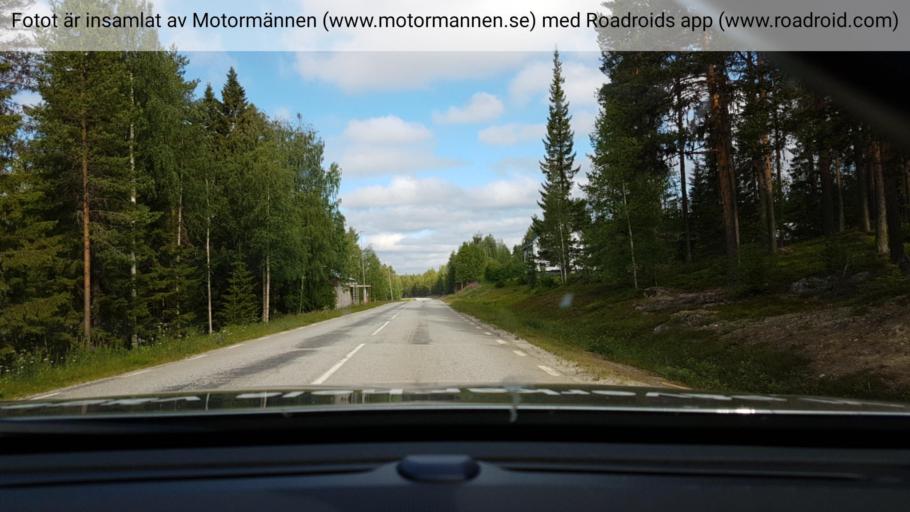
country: SE
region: Vaesterbotten
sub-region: Lycksele Kommun
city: Lycksele
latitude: 64.7751
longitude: 19.0157
